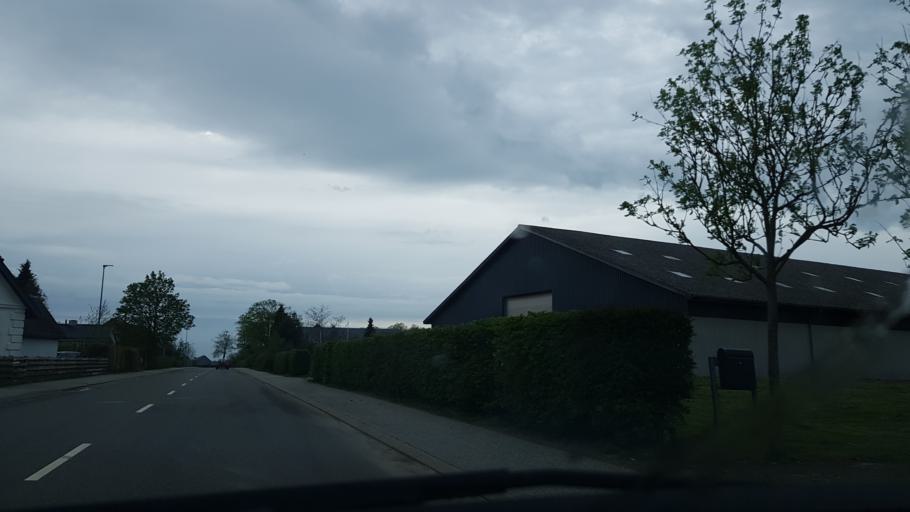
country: DK
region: South Denmark
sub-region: Kolding Kommune
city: Lunderskov
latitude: 55.4636
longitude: 9.3400
